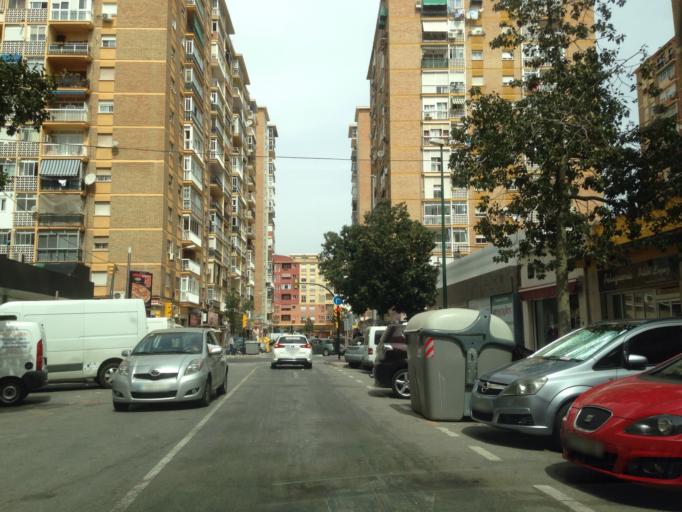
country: ES
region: Andalusia
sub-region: Provincia de Malaga
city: Malaga
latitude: 36.7056
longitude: -4.4357
